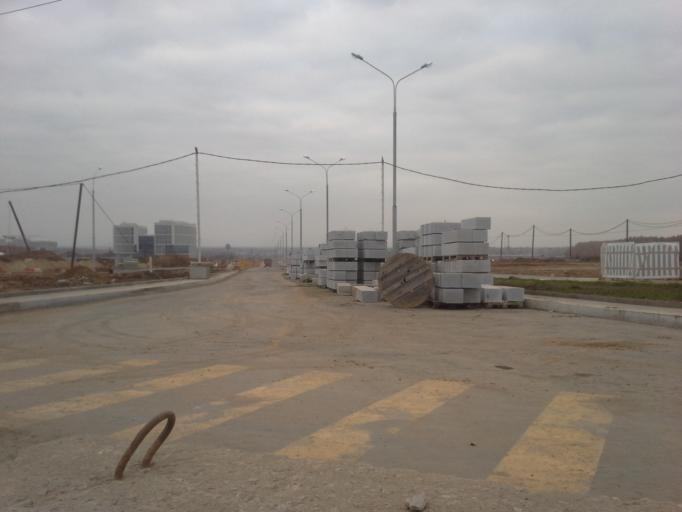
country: RU
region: Moskovskaya
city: Kommunarka
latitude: 55.5787
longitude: 37.4695
